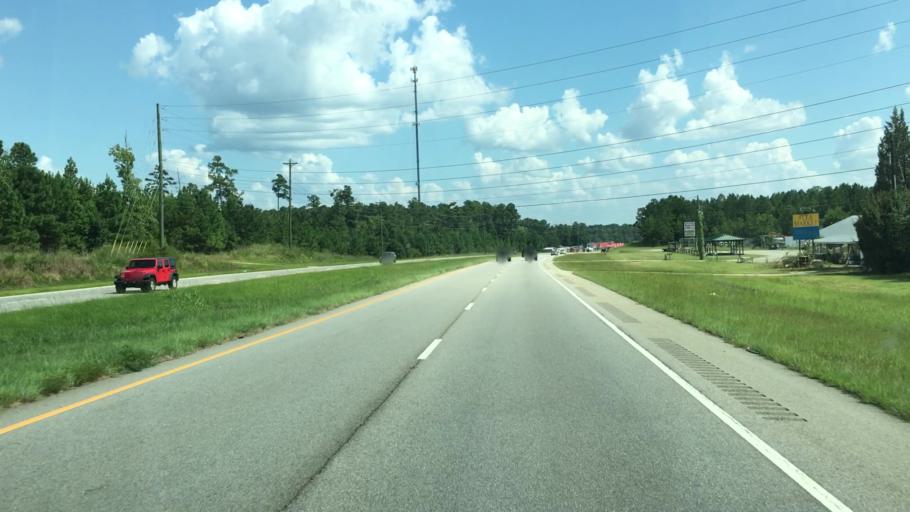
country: US
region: Georgia
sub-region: Putnam County
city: Eatonton
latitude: 33.2115
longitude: -83.3006
